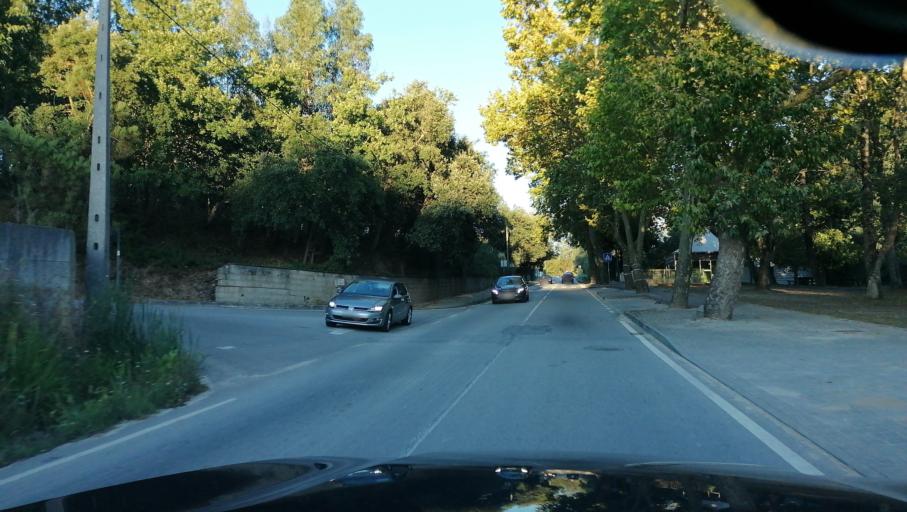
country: PT
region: Aveiro
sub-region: Agueda
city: Agueda
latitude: 40.5572
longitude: -8.4796
